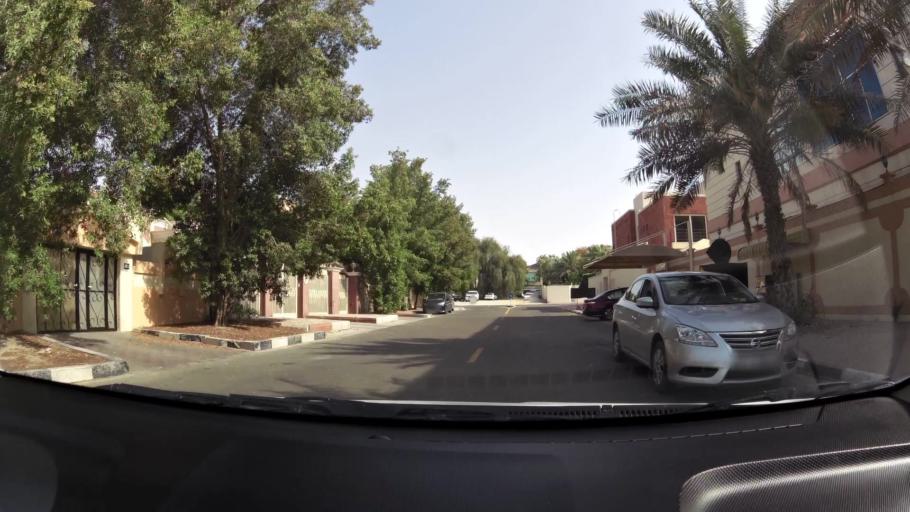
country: AE
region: Ash Shariqah
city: Sharjah
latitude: 25.2449
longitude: 55.3517
